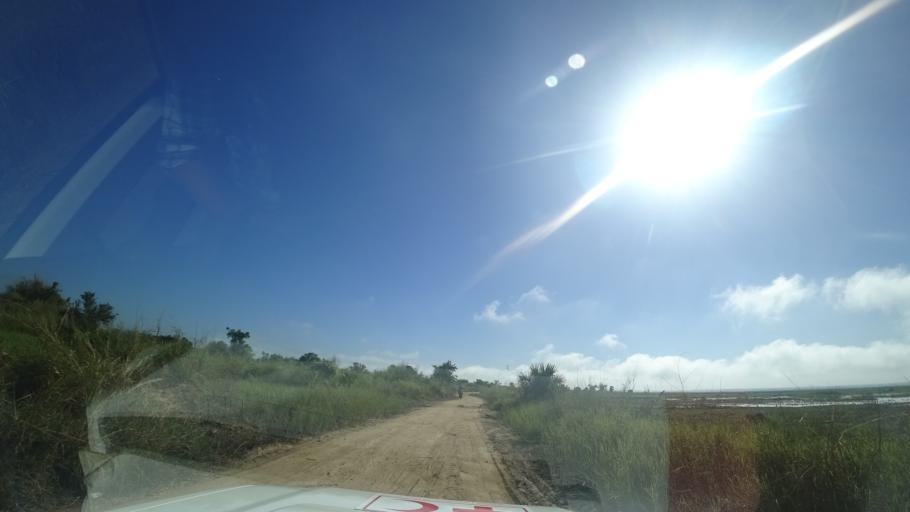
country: MZ
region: Sofala
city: Dondo
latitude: -19.4267
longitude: 34.5614
